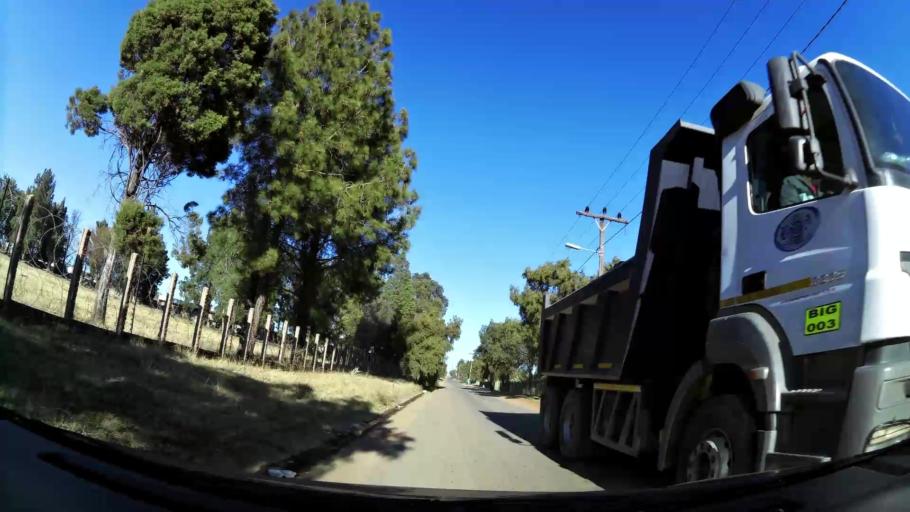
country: ZA
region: Gauteng
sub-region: City of Johannesburg Metropolitan Municipality
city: Midrand
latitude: -26.0331
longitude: 28.1458
